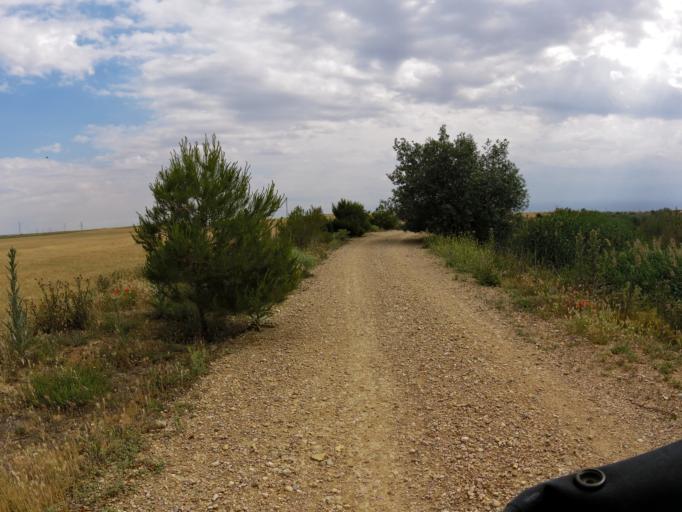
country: ES
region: Castille-La Mancha
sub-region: Provincia de Albacete
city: Albacete
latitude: 39.0381
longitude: -1.7873
